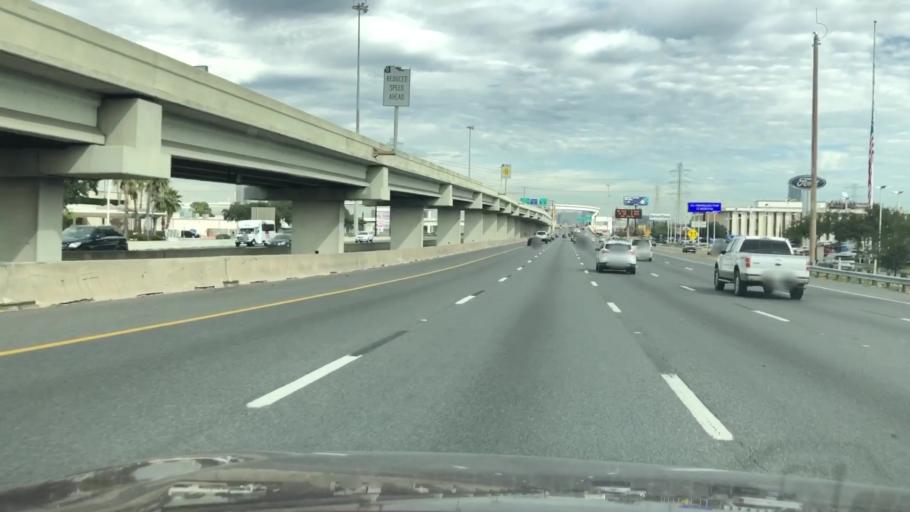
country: US
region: Texas
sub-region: Harris County
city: Bellaire
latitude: 29.7181
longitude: -95.4975
